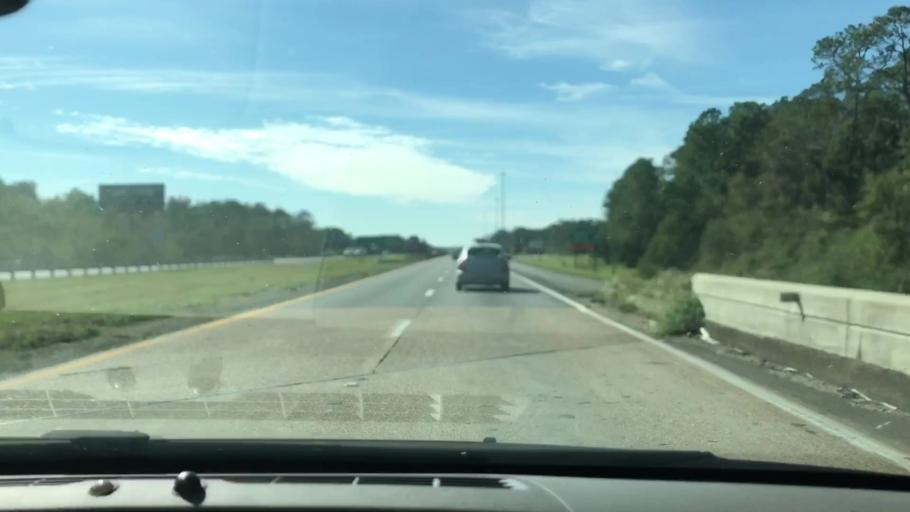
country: US
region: Alabama
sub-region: Mobile County
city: Grand Bay
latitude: 30.4749
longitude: -88.3994
